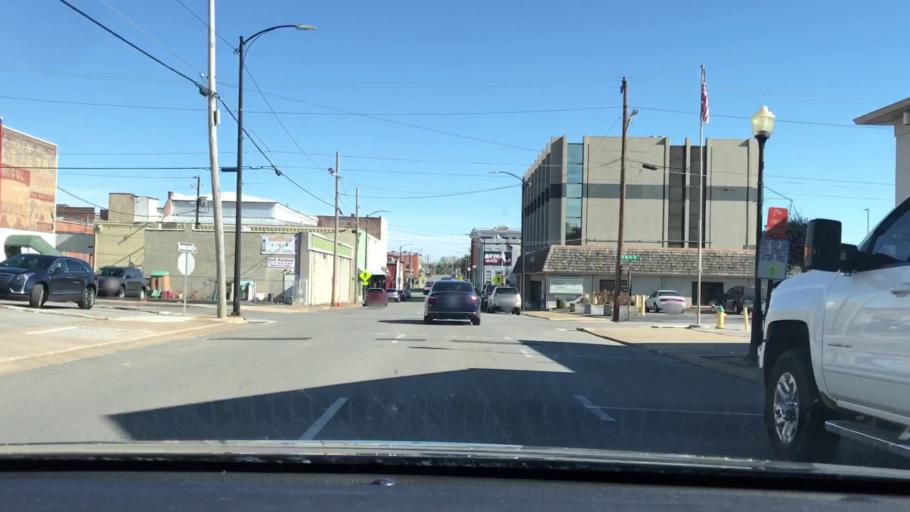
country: US
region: Kentucky
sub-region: Christian County
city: Hopkinsville
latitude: 36.8634
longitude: -87.4891
